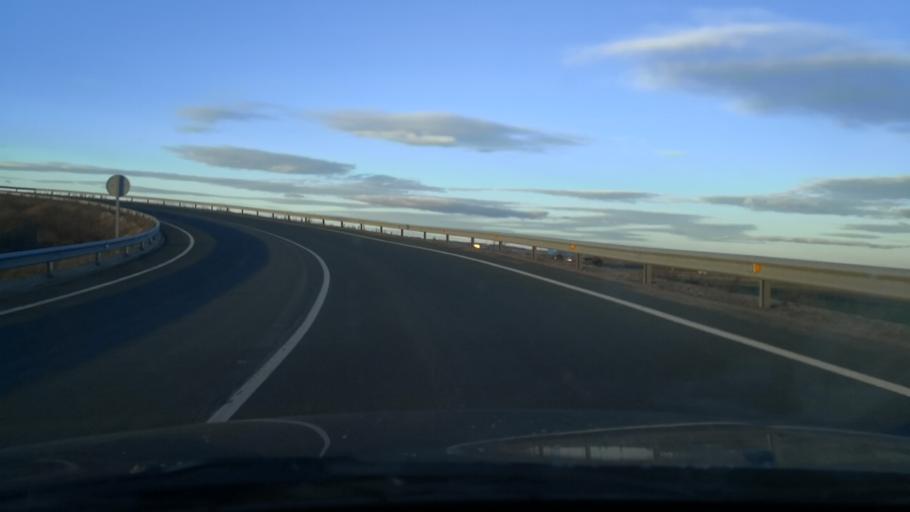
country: ES
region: Castille and Leon
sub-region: Provincia de Valladolid
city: Tordesillas
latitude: 41.4793
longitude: -4.9897
